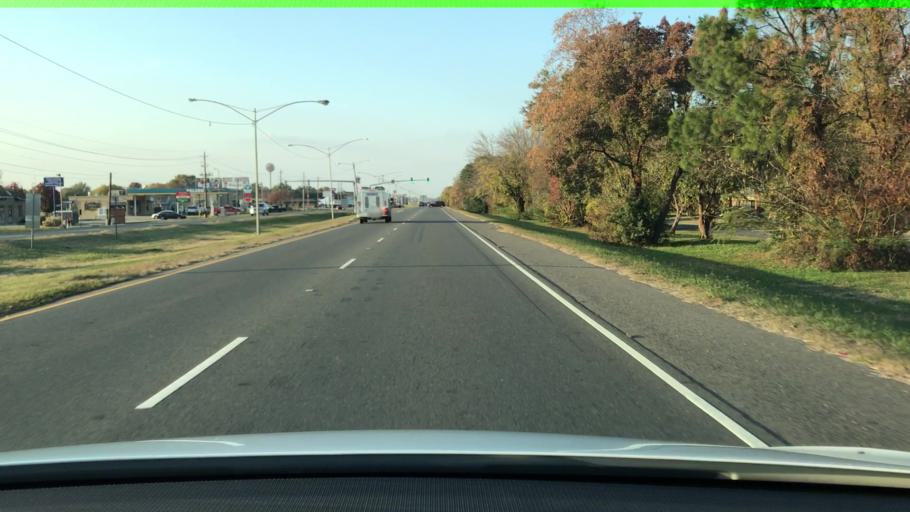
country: US
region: Louisiana
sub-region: Bossier Parish
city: Bossier City
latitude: 32.4189
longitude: -93.7043
